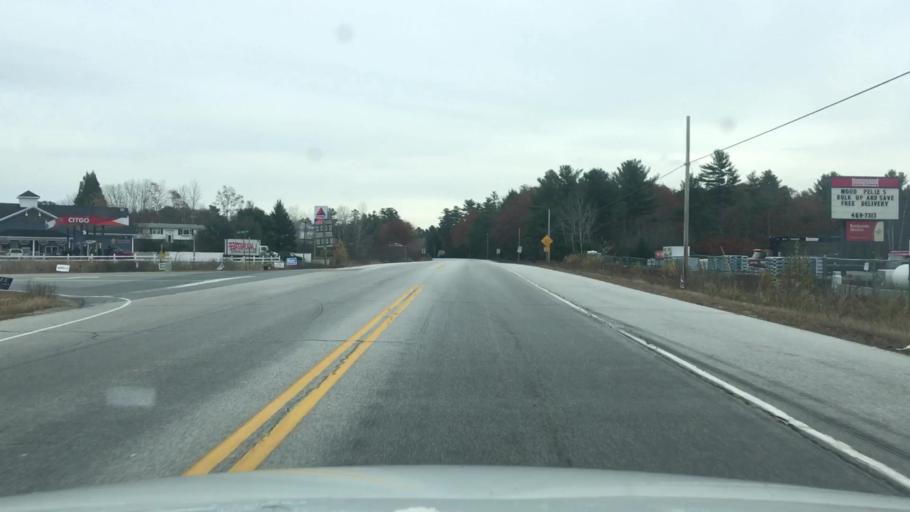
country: US
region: Maine
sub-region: Hancock County
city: Orland
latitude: 44.5700
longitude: -68.7654
